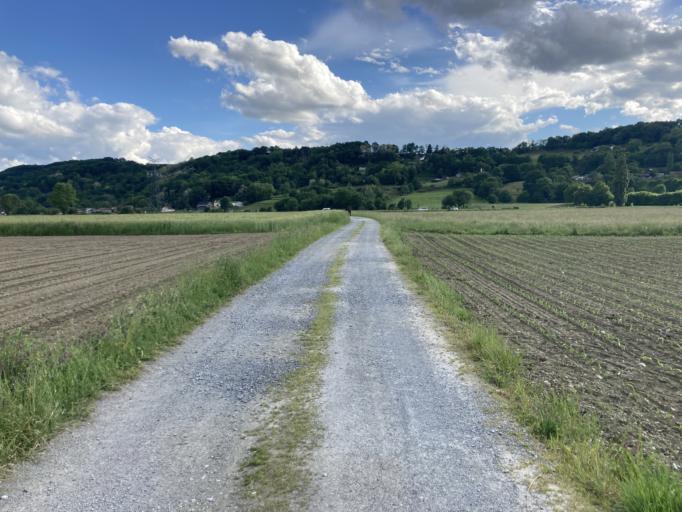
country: FR
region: Aquitaine
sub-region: Departement des Pyrenees-Atlantiques
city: Arbus
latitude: 43.3451
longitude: -0.5124
